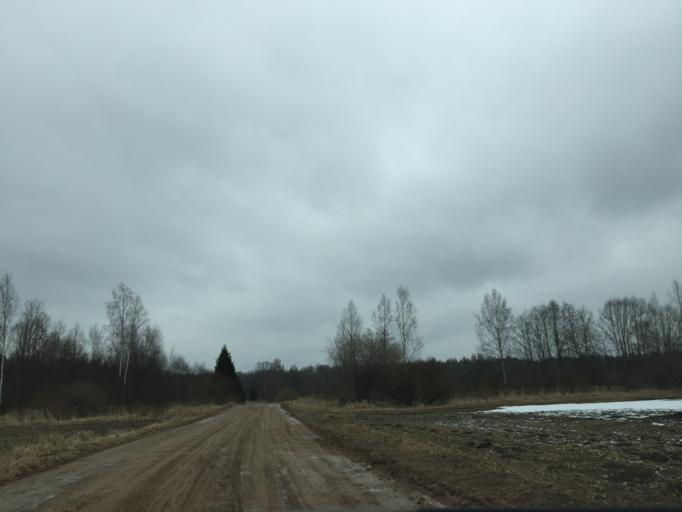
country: LV
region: Lielvarde
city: Lielvarde
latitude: 56.7575
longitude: 24.8160
